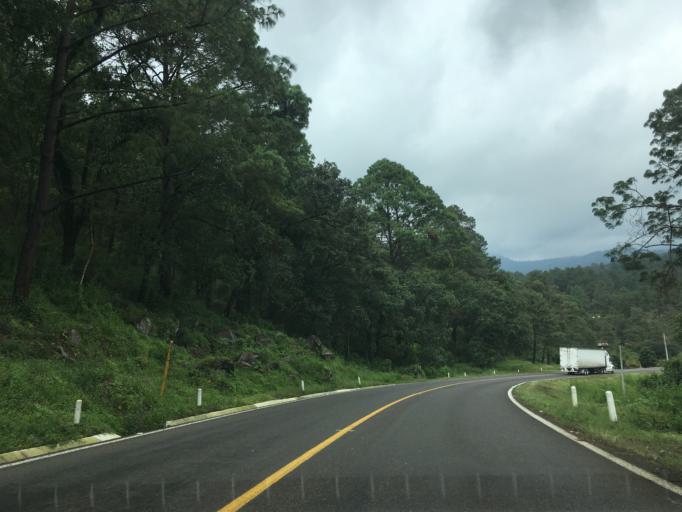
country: MX
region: Michoacan
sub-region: Uruapan
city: Toreo Bajo (El Toreo Bajo)
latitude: 19.4622
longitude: -101.9538
